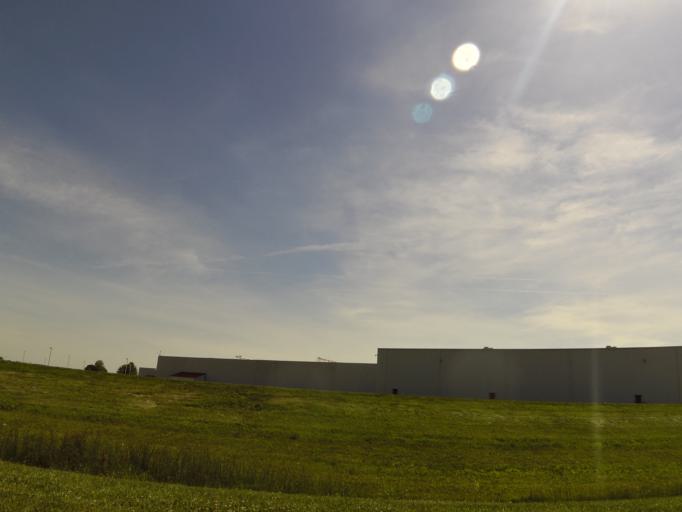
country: US
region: Illinois
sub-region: Vermilion County
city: Danville
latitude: 40.1293
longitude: -87.5503
